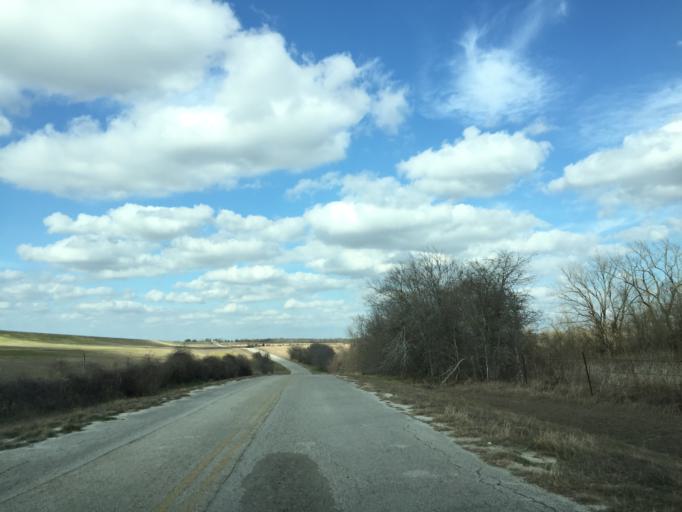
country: US
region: Texas
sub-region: Williamson County
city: Granger
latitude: 30.7028
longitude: -97.3270
